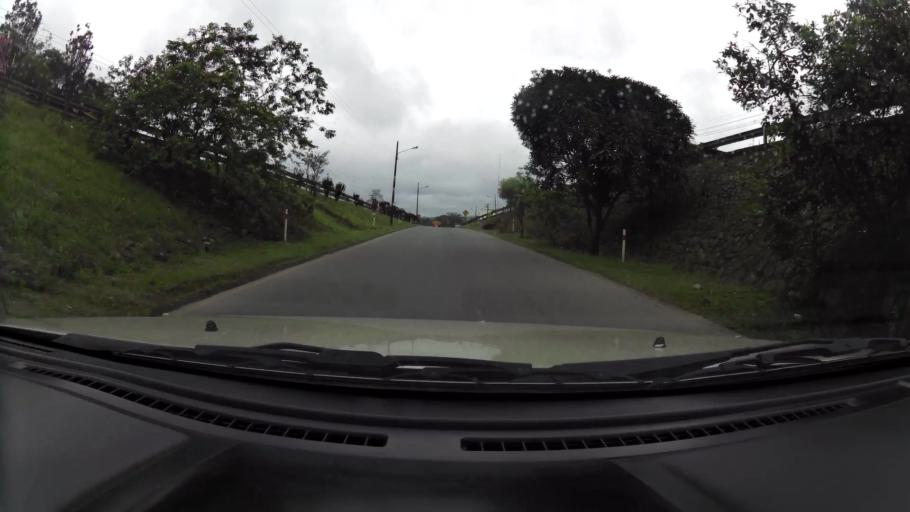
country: EC
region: Santo Domingo de los Tsachilas
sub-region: Canton Santo Domingo de los Colorados
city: Santo Domingo de los Colorados
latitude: -0.2469
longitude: -79.1451
